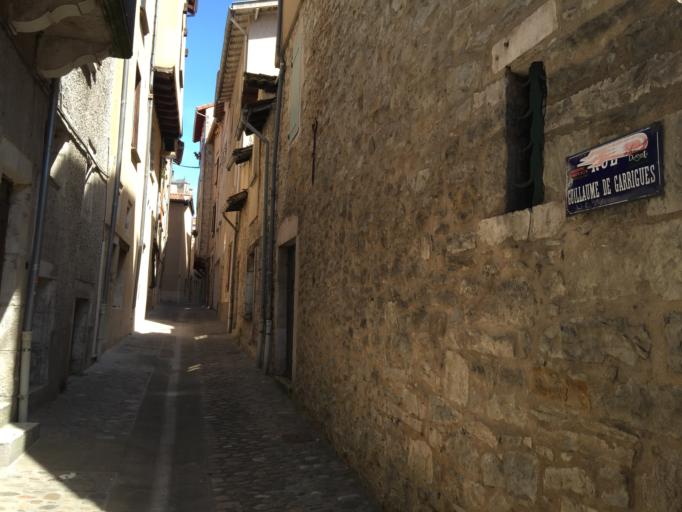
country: FR
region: Midi-Pyrenees
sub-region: Departement de l'Aveyron
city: Villefranche-de-Rouergue
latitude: 44.3495
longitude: 2.0375
